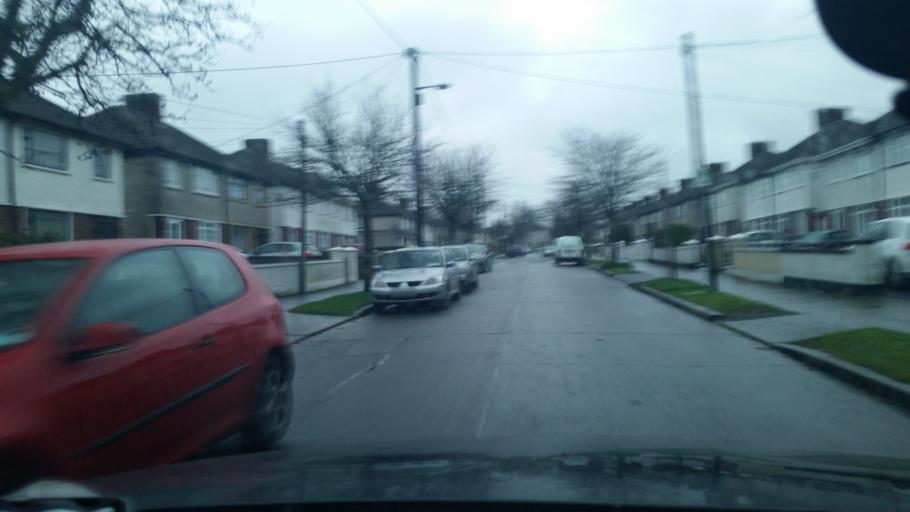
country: IE
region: Leinster
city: Marino
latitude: 53.3821
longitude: -6.2293
